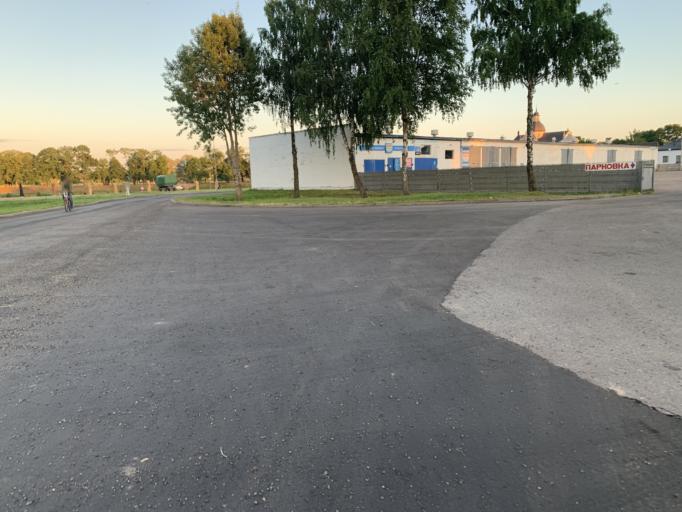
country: BY
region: Minsk
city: Nyasvizh
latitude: 53.2243
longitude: 26.6847
